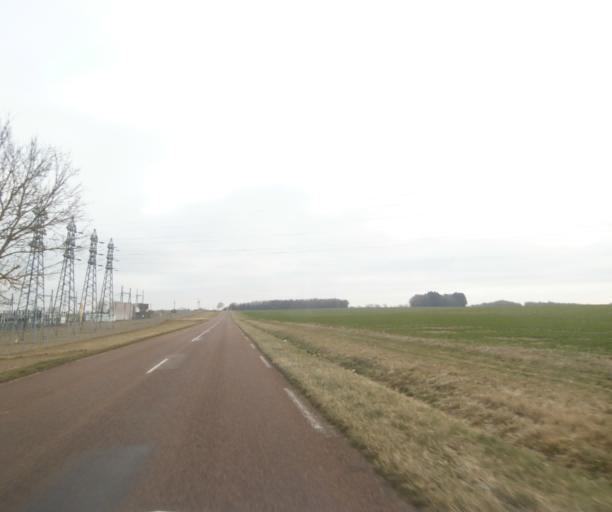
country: FR
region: Champagne-Ardenne
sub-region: Departement de la Haute-Marne
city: Chancenay
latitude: 48.6752
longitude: 4.9971
